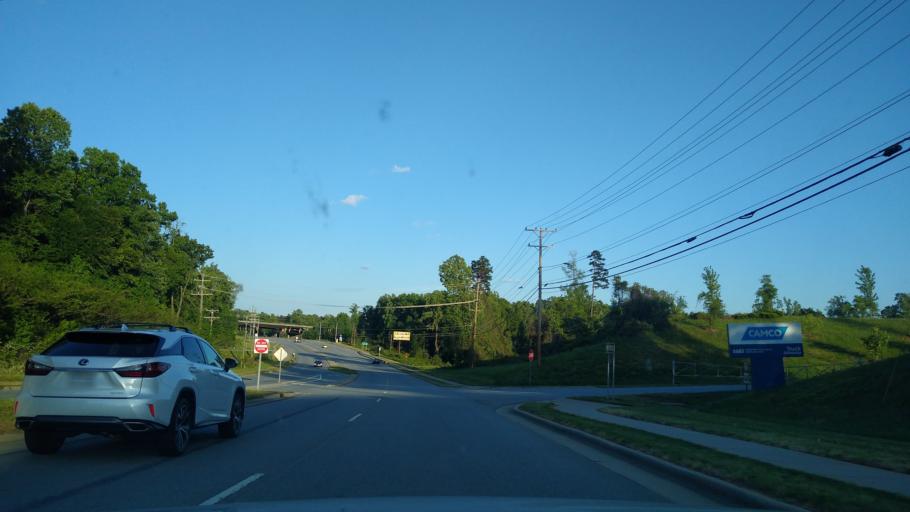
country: US
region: North Carolina
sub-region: Guilford County
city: Oak Ridge
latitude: 36.0958
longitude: -79.9718
